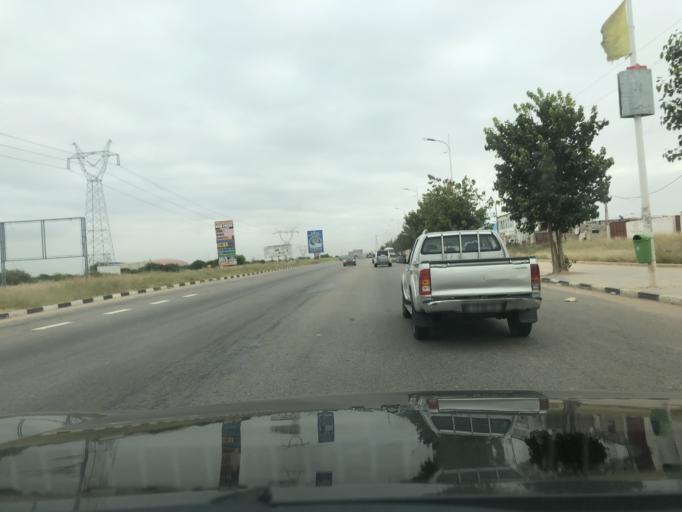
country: AO
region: Luanda
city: Luanda
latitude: -8.9832
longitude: 13.2902
